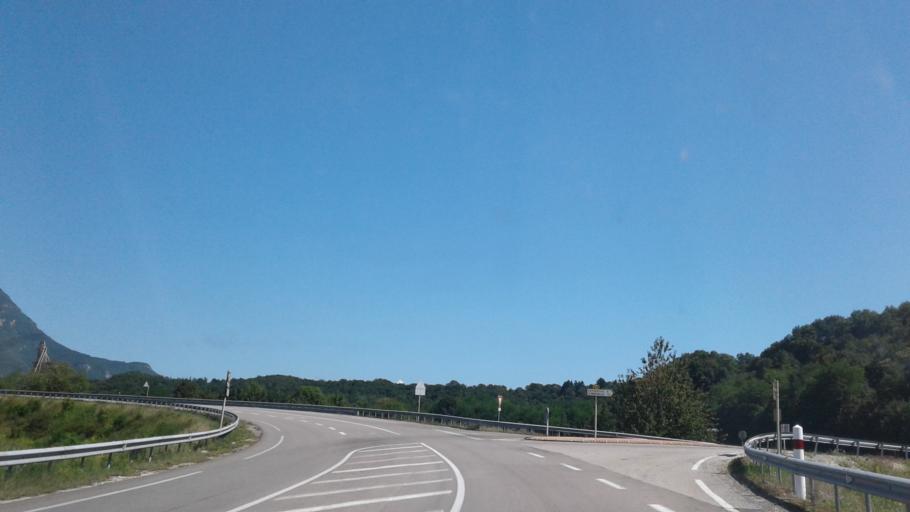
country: FR
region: Rhone-Alpes
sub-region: Departement de l'Ain
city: Artemare
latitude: 45.8615
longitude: 5.6778
